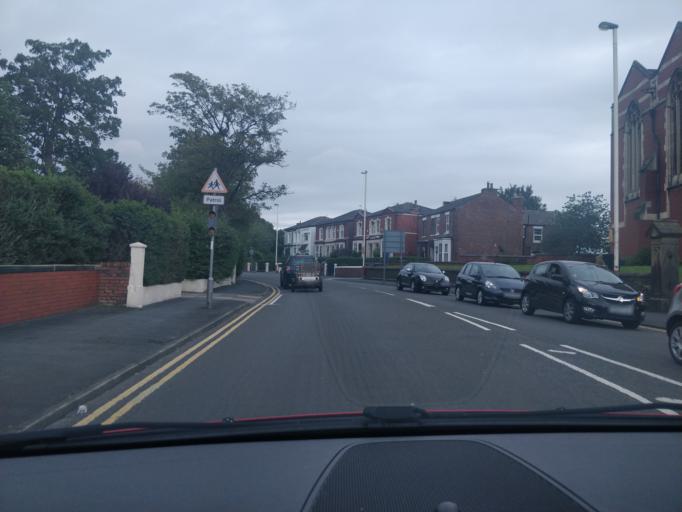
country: GB
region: England
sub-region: Sefton
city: Southport
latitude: 53.6506
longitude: -2.9966
